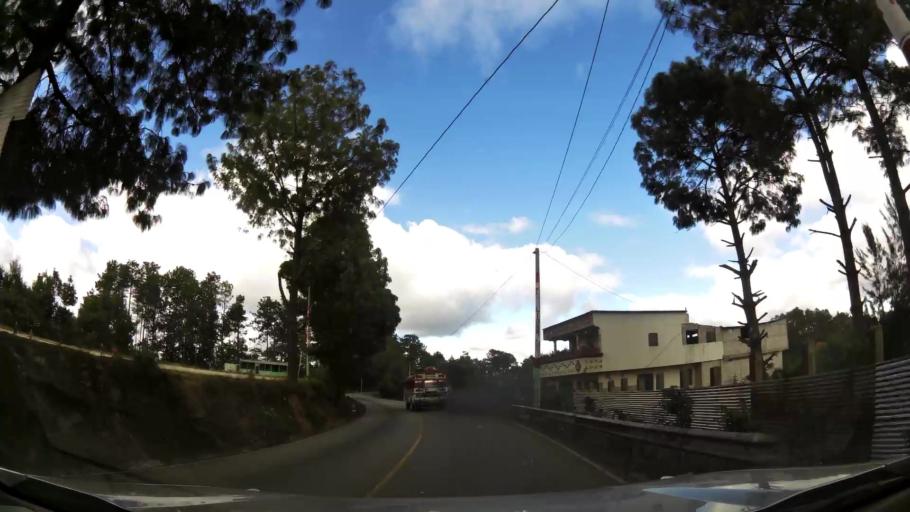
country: GT
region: Quiche
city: Chichicastenango
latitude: 14.9116
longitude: -91.1060
